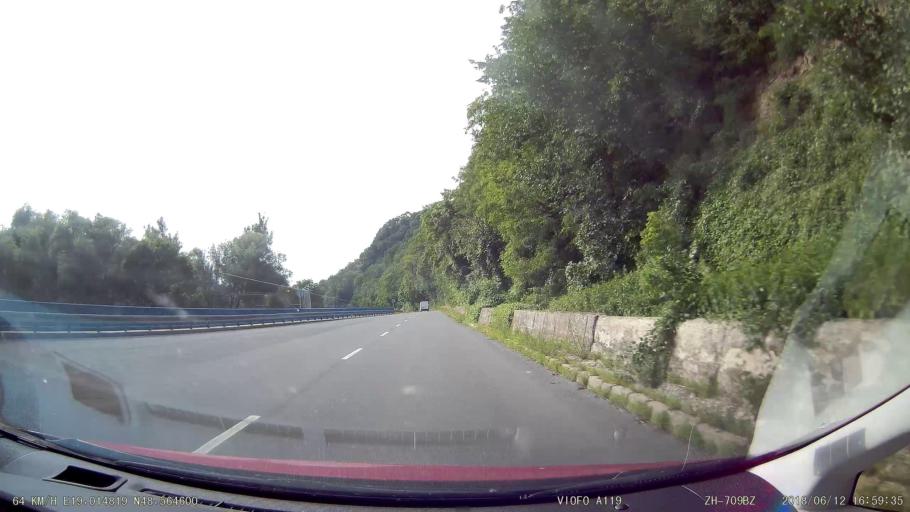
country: SK
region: Banskobystricky
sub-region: Okres Banska Bystrica
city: Zvolen
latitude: 48.5647
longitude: 19.0147
